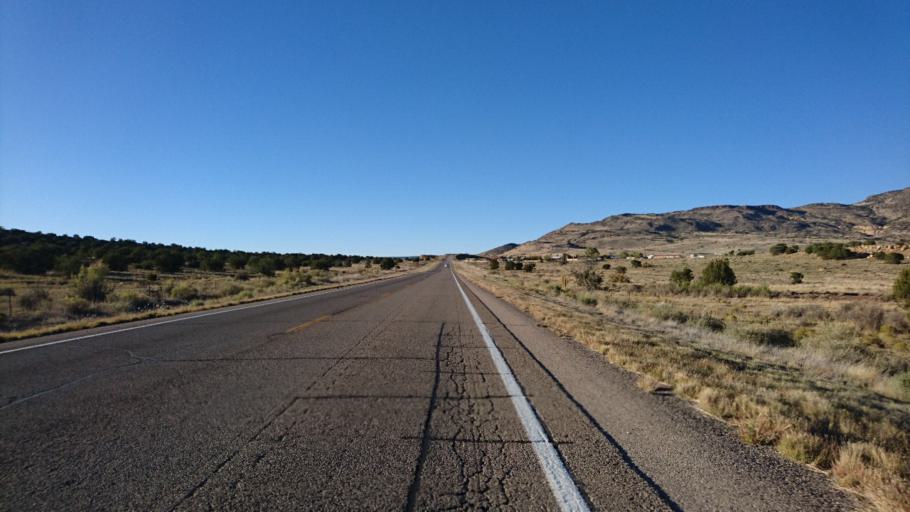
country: US
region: New Mexico
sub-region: Cibola County
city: Grants
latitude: 35.0989
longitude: -107.7746
